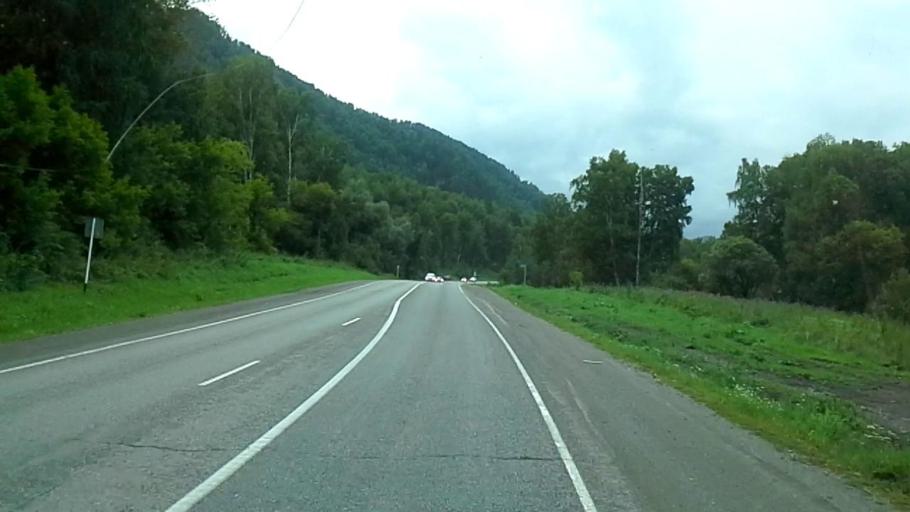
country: RU
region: Altay
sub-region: Mayminskiy Rayon
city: Manzherok
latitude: 51.8619
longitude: 85.7606
